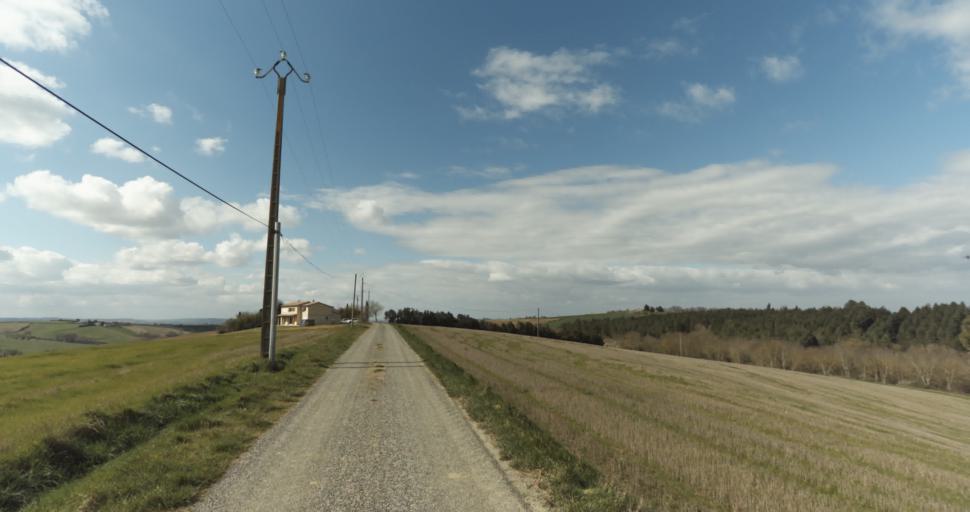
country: FR
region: Midi-Pyrenees
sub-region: Departement de la Haute-Garonne
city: Auterive
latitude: 43.3680
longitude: 1.5065
